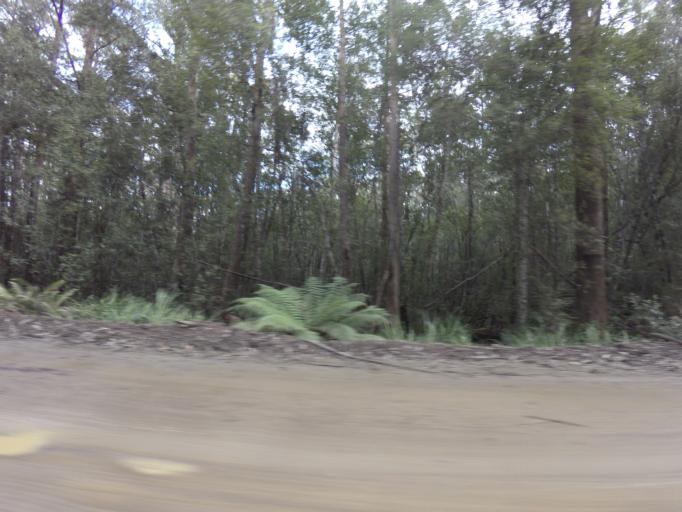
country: AU
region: Tasmania
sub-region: Huon Valley
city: Geeveston
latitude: -43.4947
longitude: 146.8804
